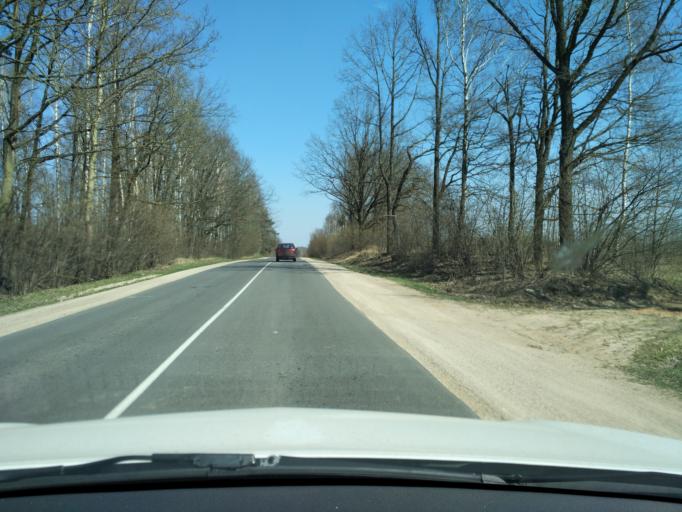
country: BY
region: Minsk
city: Slabada
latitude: 53.9934
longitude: 27.9738
